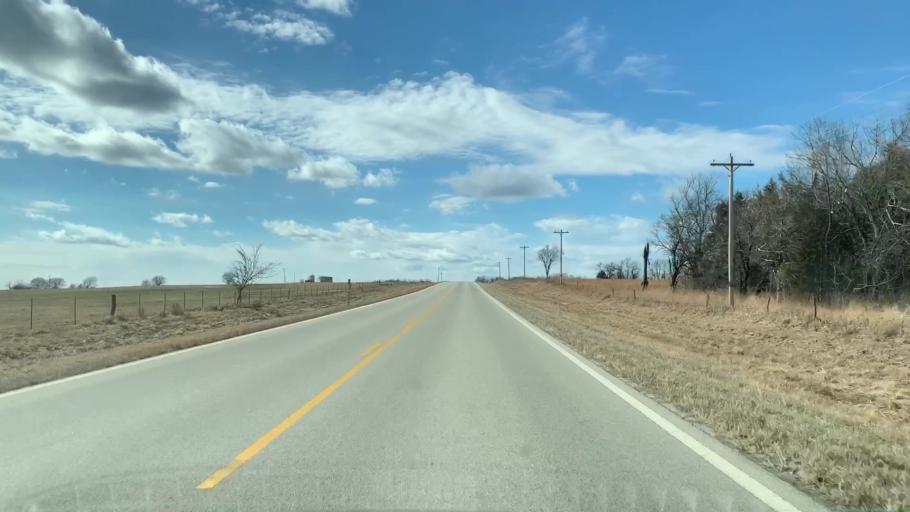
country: US
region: Kansas
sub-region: Neosho County
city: Chanute
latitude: 37.5289
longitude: -95.4300
